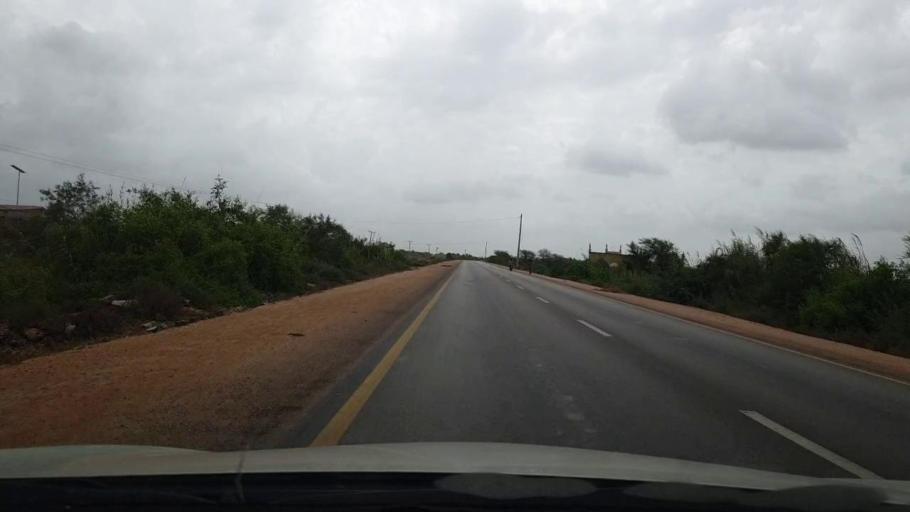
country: PK
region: Sindh
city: Mirpur Batoro
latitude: 24.6243
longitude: 68.3316
